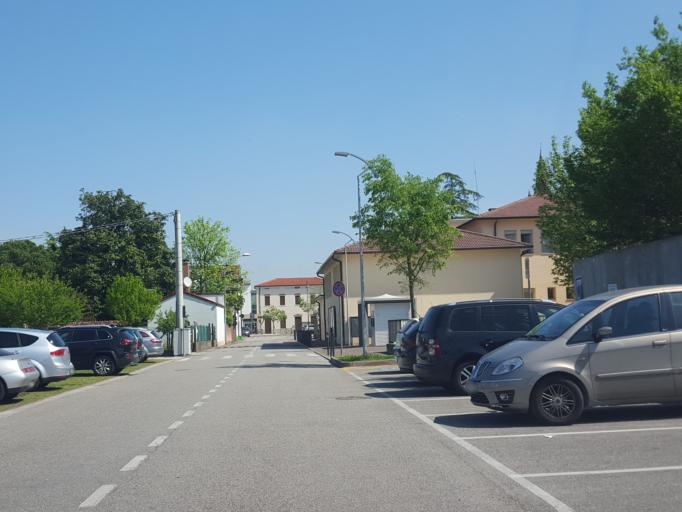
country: IT
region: Veneto
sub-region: Provincia di Vicenza
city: Torri di Quartesolo
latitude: 45.5191
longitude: 11.6146
